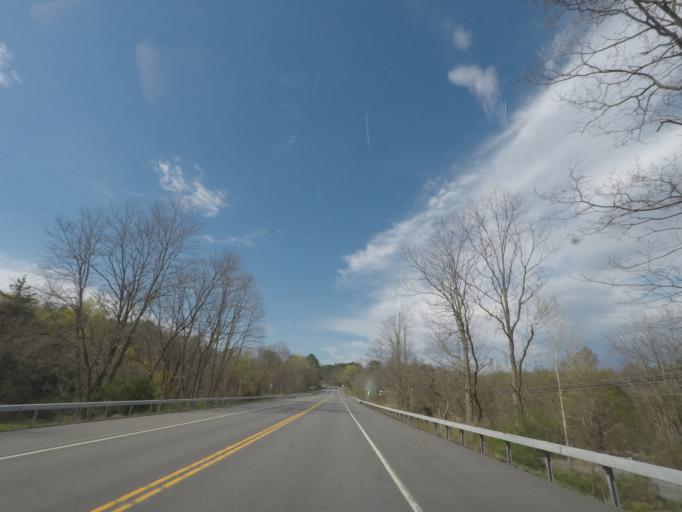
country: US
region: New York
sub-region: Greene County
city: Cairo
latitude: 42.3200
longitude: -74.0125
